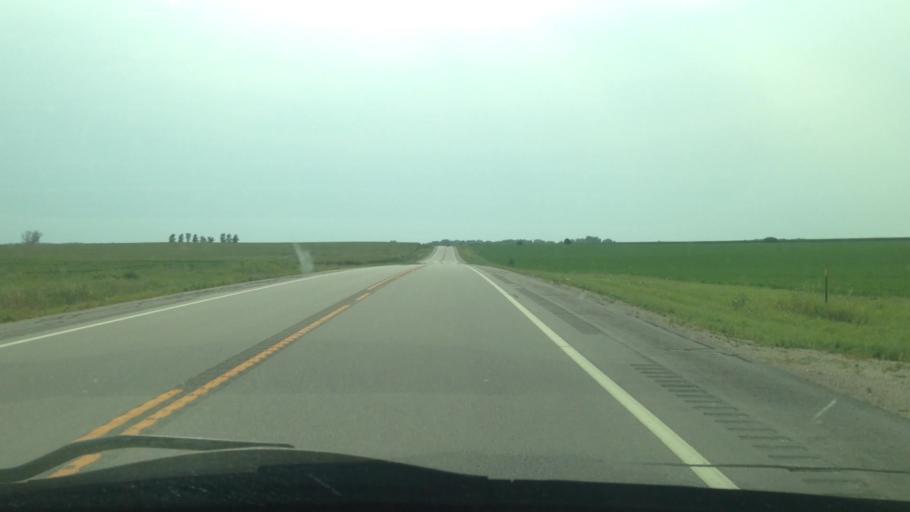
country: US
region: Minnesota
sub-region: Olmsted County
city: Eyota
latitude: 43.9993
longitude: -92.2666
